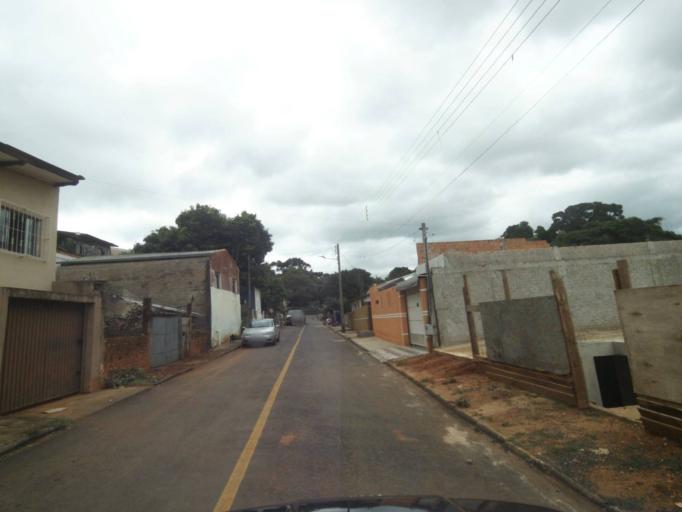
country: BR
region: Parana
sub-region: Telemaco Borba
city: Telemaco Borba
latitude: -24.3262
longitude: -50.6377
